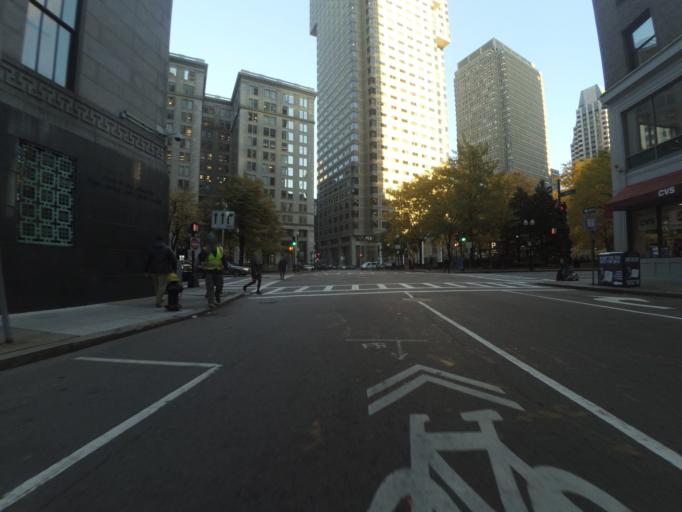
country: US
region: Massachusetts
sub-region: Suffolk County
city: Boston
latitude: 42.3574
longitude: -71.0577
